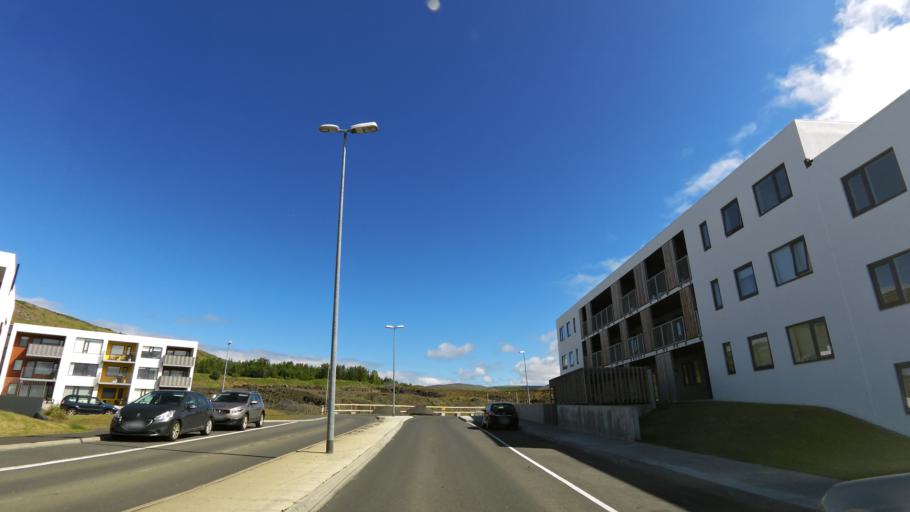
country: IS
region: Capital Region
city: Mosfellsbaer
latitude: 64.1672
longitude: -21.6620
